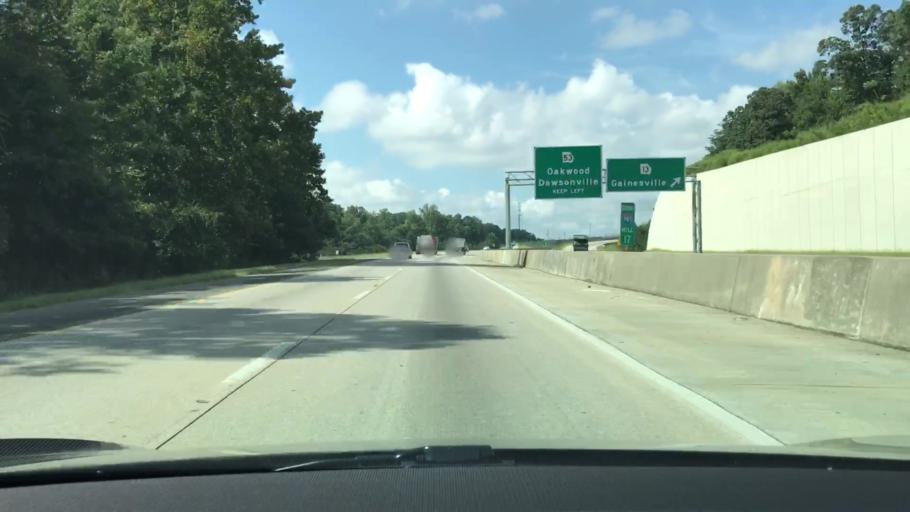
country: US
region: Georgia
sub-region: Hall County
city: Oakwood
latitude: 34.2326
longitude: -83.8509
